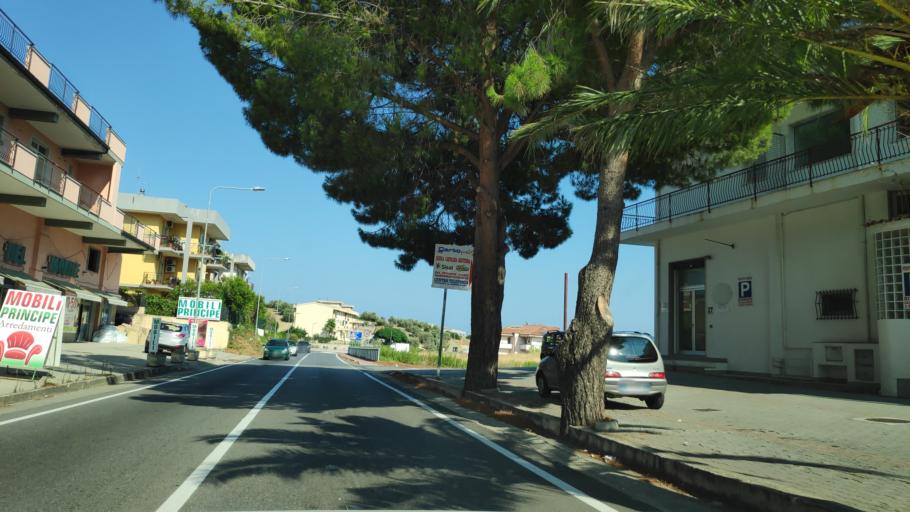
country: IT
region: Calabria
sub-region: Provincia di Catanzaro
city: Martelli-Laganosa
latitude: 38.6797
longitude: 16.5407
